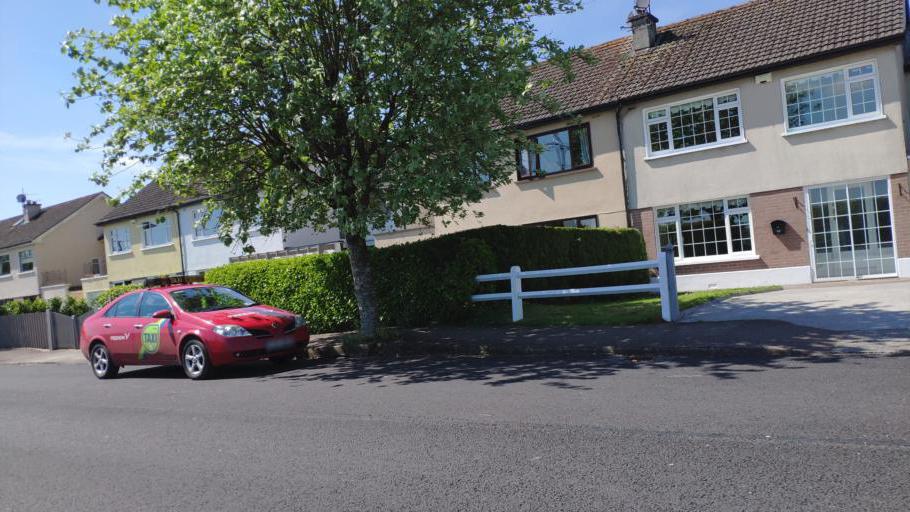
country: IE
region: Munster
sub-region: County Cork
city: Blarney
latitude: 51.9302
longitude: -8.5589
